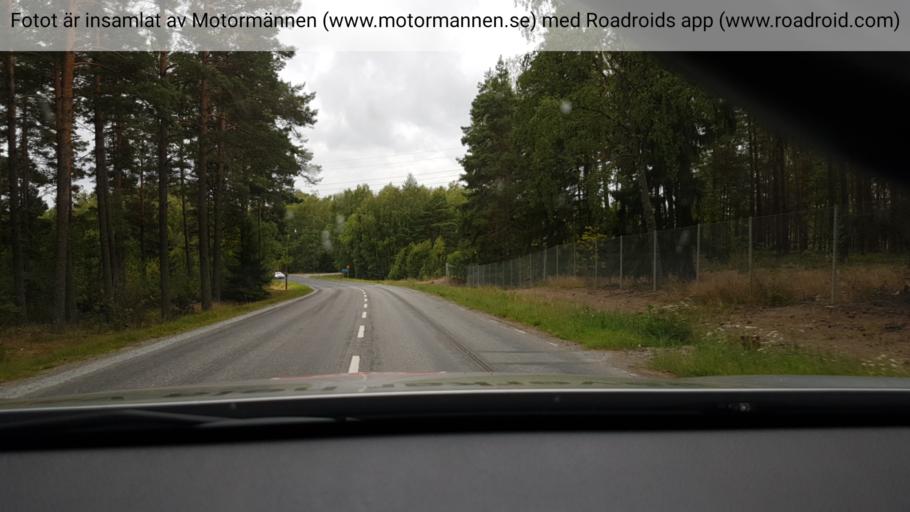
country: SE
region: Stockholm
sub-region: Sigtuna Kommun
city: Rosersberg
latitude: 59.6067
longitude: 17.9137
